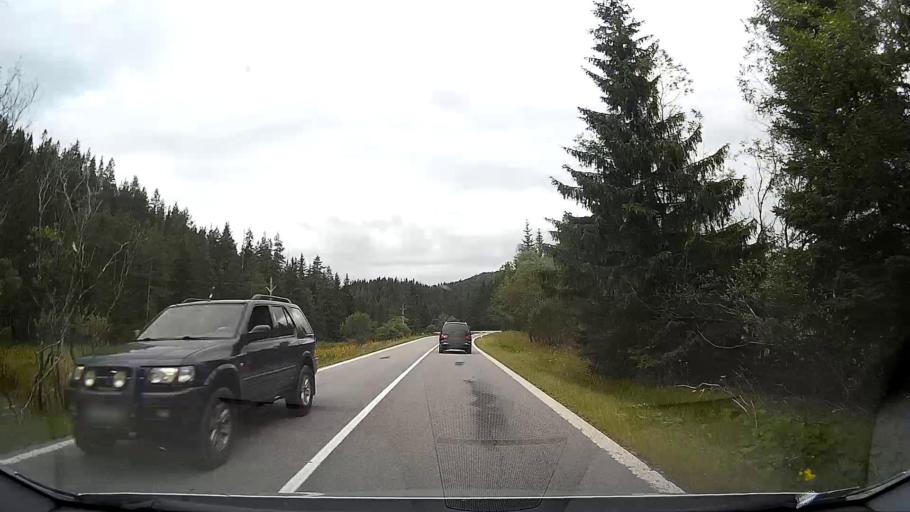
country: SK
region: Kosicky
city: Dobsina
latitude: 48.8790
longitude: 20.2309
